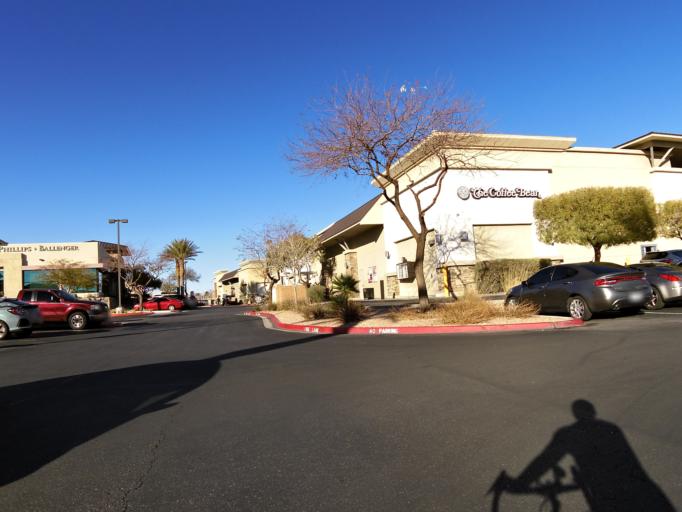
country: US
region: Nevada
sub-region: Clark County
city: Summerlin South
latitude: 36.1240
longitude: -115.3258
